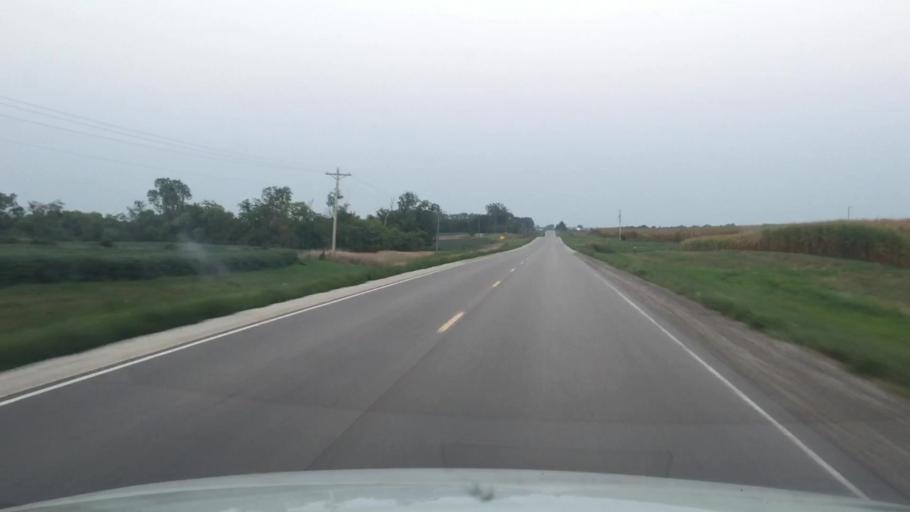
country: US
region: Iowa
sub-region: Warren County
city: Indianola
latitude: 41.1827
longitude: -93.4911
